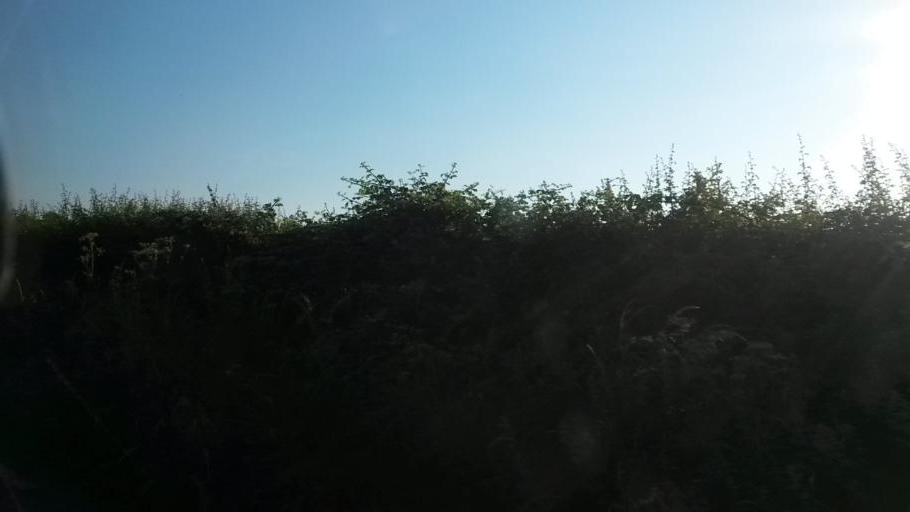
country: IE
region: Leinster
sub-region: An Mhi
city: Ashbourne
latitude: 53.5567
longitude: -6.3817
